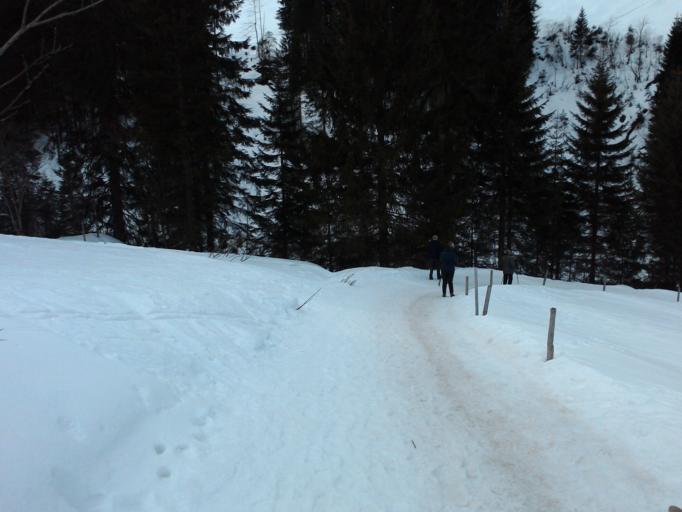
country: AT
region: Vorarlberg
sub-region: Politischer Bezirk Bregenz
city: Mittelberg
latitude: 47.3038
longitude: 10.1184
